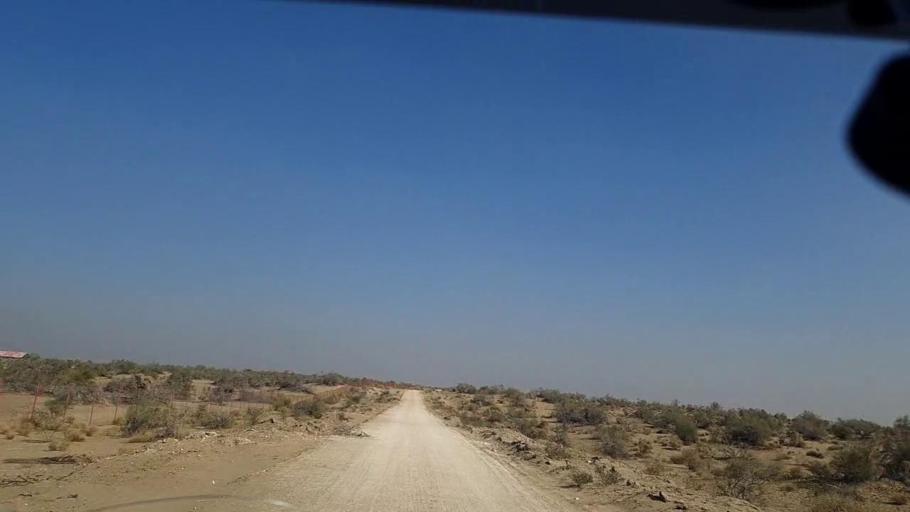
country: PK
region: Sindh
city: Khanpur
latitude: 27.5576
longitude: 69.3927
